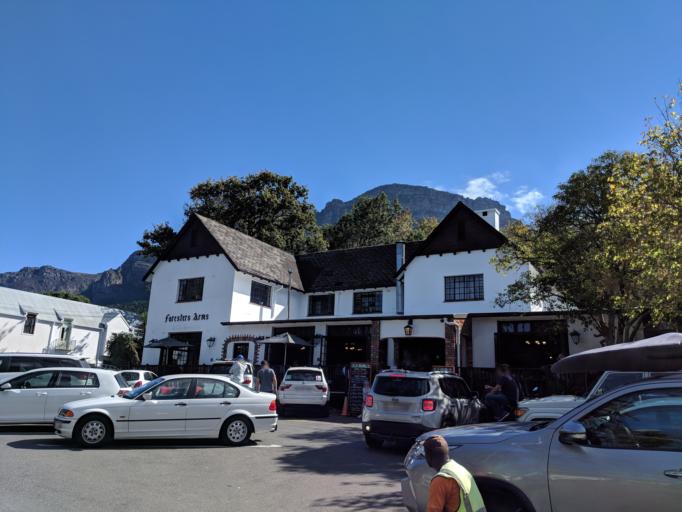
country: ZA
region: Western Cape
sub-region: City of Cape Town
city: Newlands
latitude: -33.9715
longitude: 18.4541
